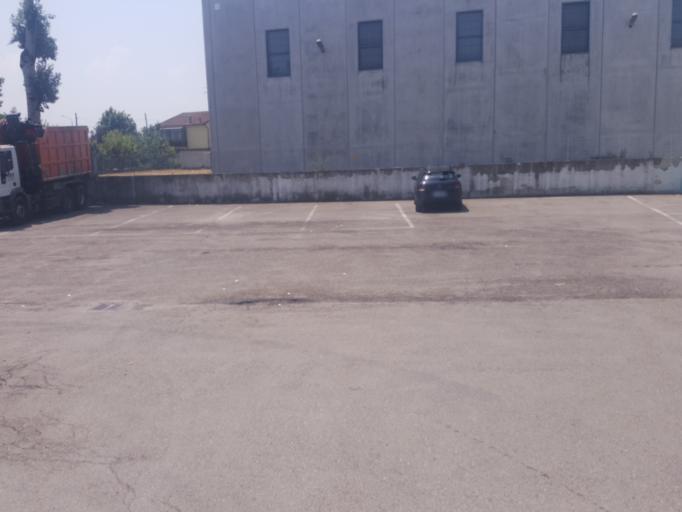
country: IT
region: Emilia-Romagna
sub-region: Provincia di Modena
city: Cavazzona
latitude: 44.5739
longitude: 11.1130
